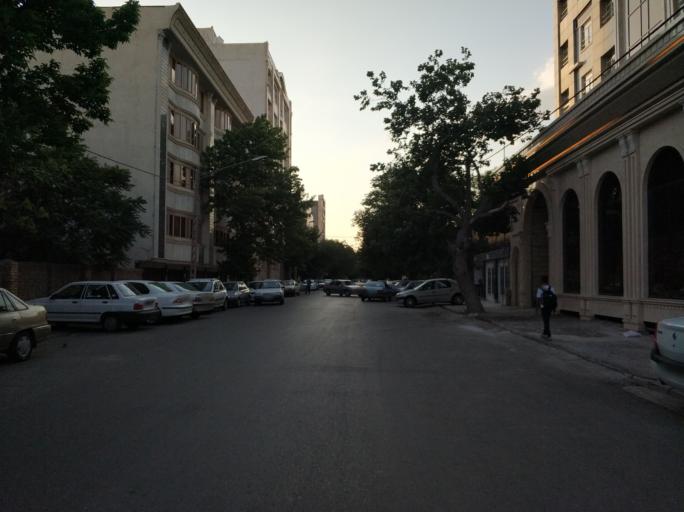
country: IR
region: Razavi Khorasan
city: Mashhad
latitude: 36.2702
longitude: 59.5997
